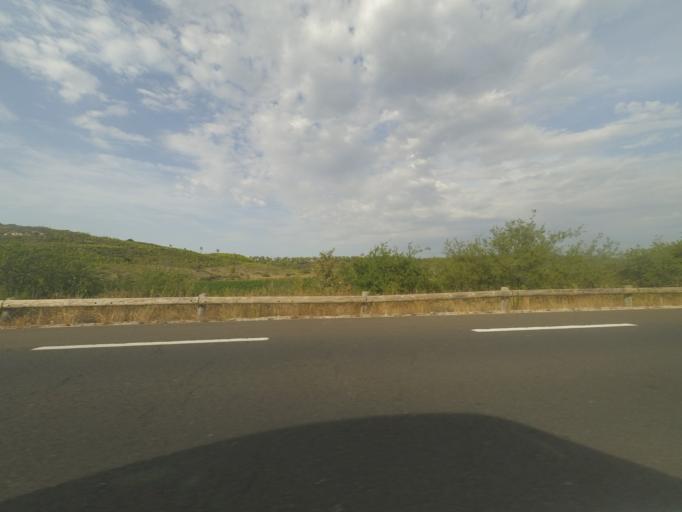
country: FR
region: Languedoc-Roussillon
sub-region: Departement de l'Herault
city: Assas
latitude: 43.7151
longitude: 3.9155
